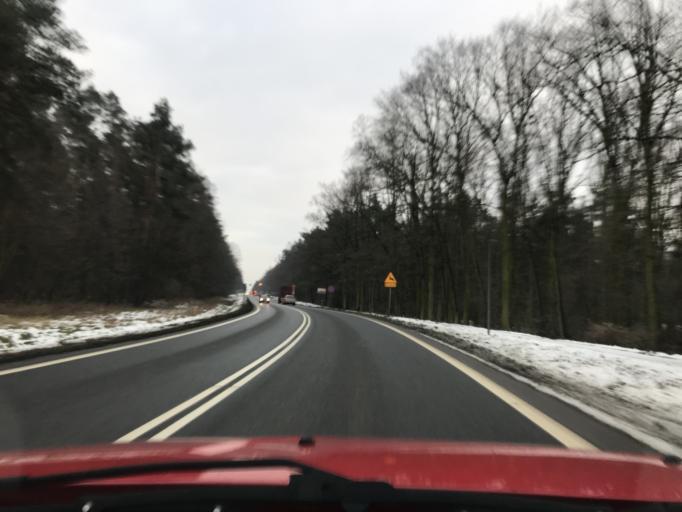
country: PL
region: Greater Poland Voivodeship
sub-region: Powiat pleszewski
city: Goluchow
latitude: 51.8468
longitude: 17.9384
